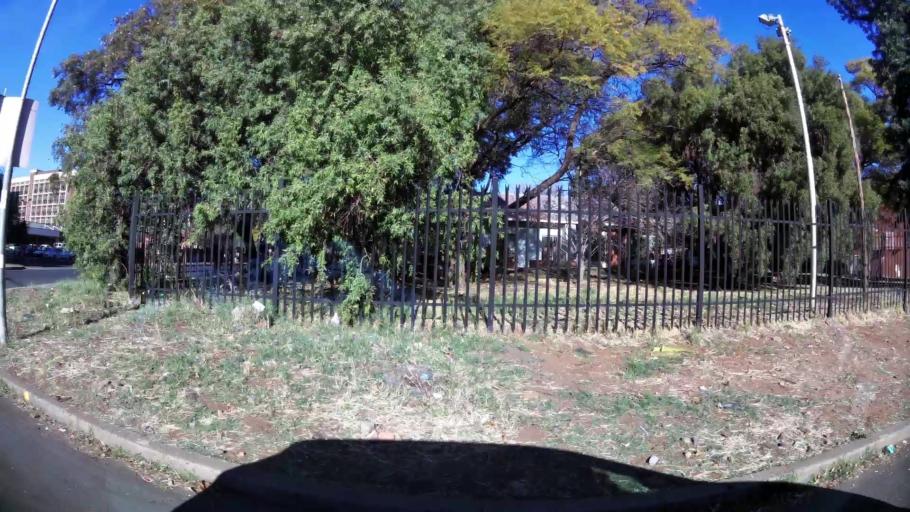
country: ZA
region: Northern Cape
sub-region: Frances Baard District Municipality
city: Kimberley
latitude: -28.7450
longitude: 24.7708
